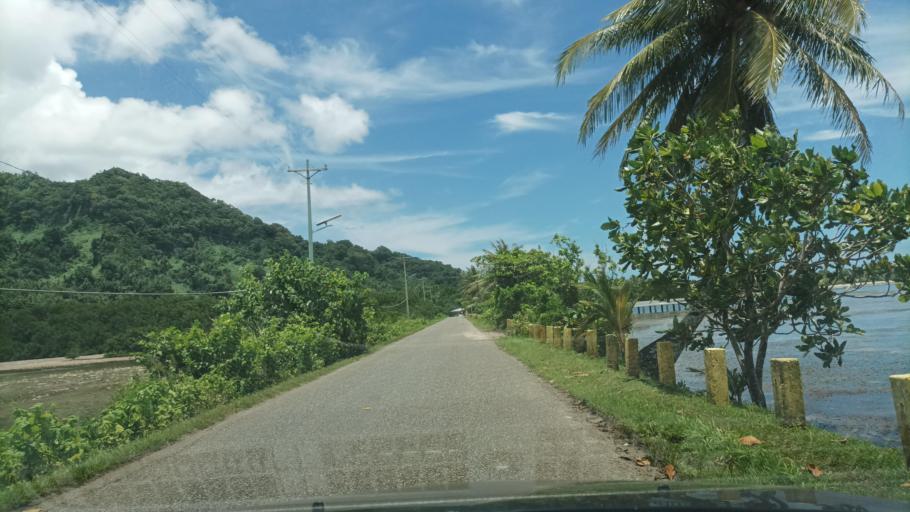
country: FM
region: Kosrae
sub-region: Lelu Municipality
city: Lelu
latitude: 5.3378
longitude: 163.0206
